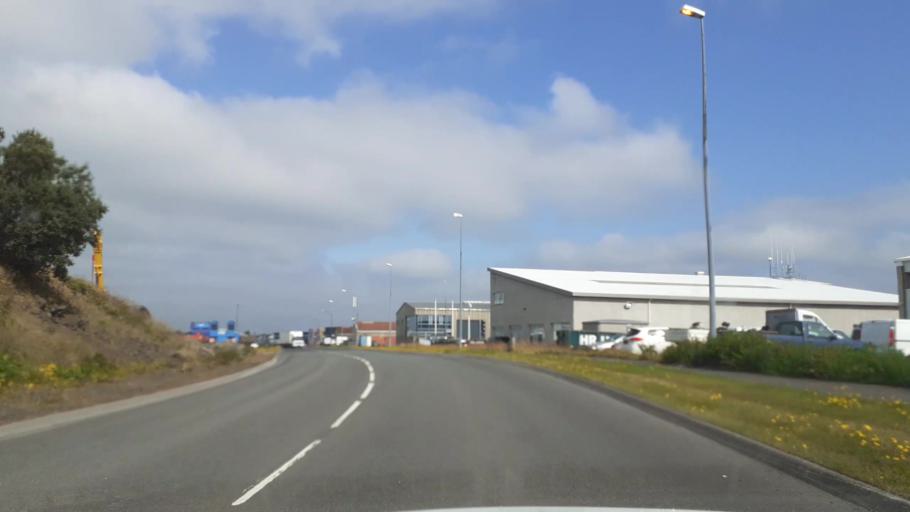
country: IS
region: Capital Region
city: Gardabaer
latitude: 64.0766
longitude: -21.9253
